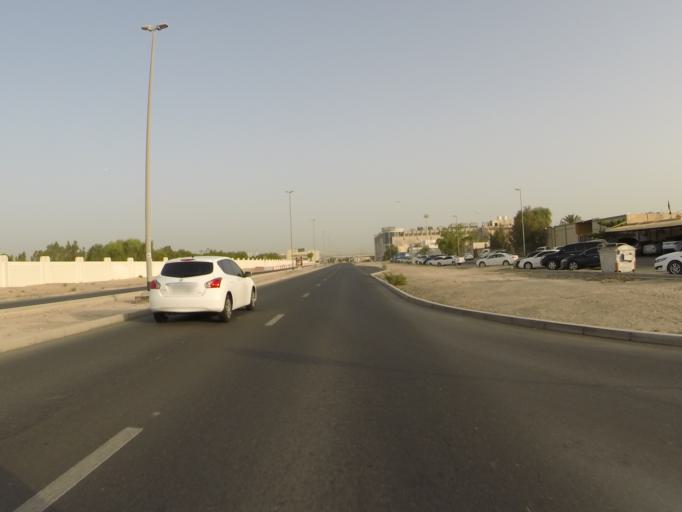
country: AE
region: Dubai
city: Dubai
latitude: 25.1658
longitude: 55.2448
